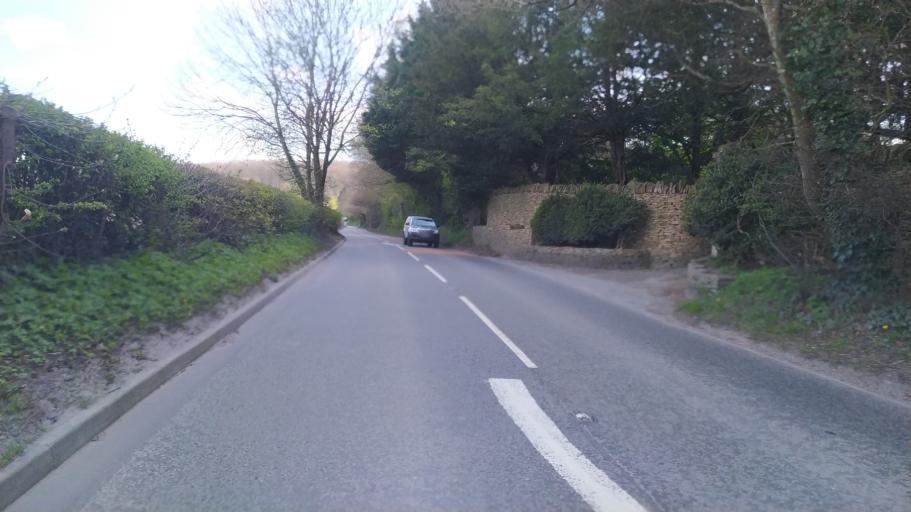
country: GB
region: England
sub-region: Wiltshire
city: Corsley
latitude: 51.2021
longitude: -2.2420
